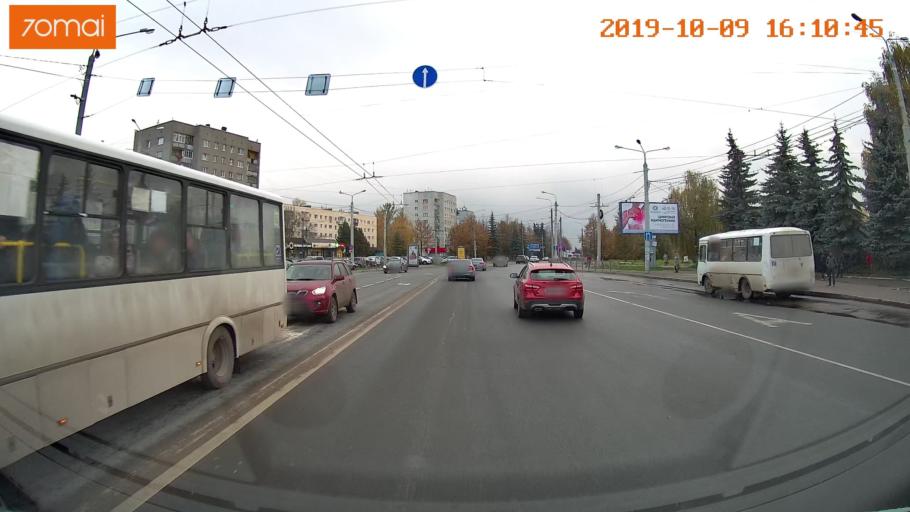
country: RU
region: Kostroma
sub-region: Kostromskoy Rayon
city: Kostroma
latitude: 57.7611
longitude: 40.9509
